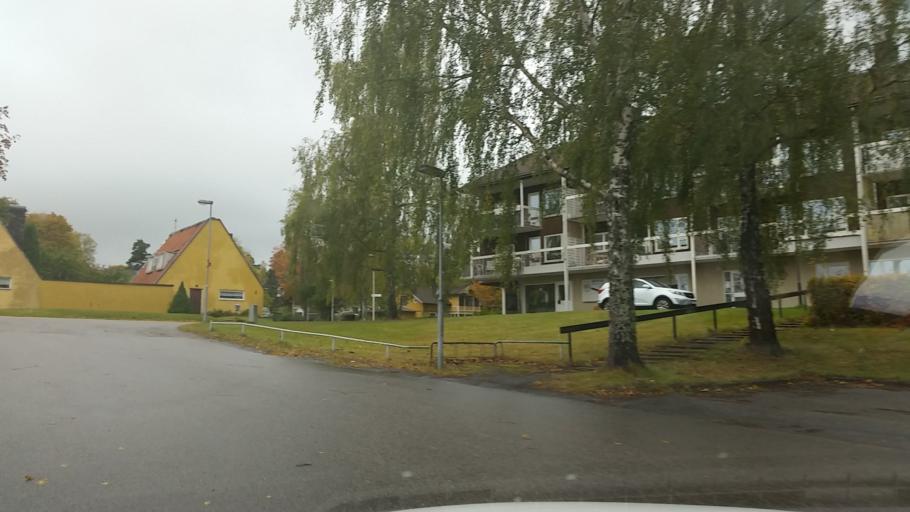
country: SE
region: Gaevleborg
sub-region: Sandvikens Kommun
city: Arsunda
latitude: 60.5430
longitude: 16.5677
